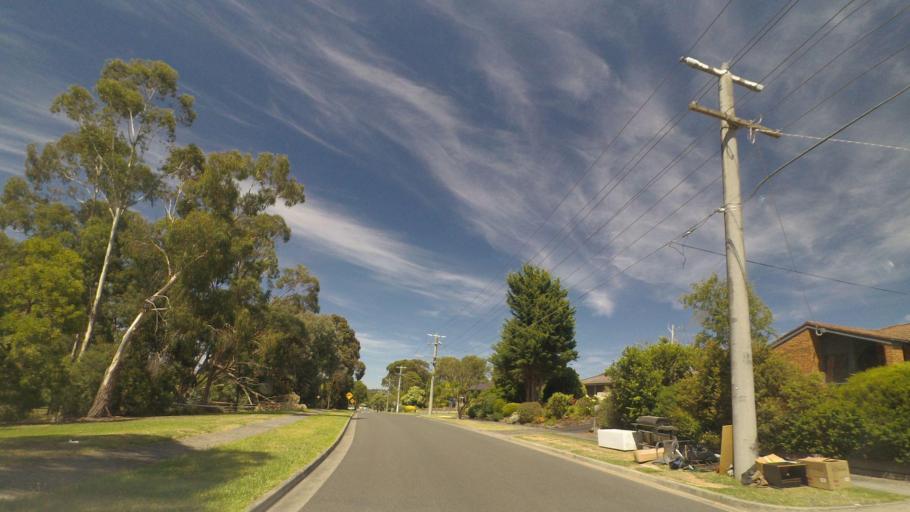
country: AU
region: Victoria
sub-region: Maroondah
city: Croydon North
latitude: -37.7710
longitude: 145.3075
